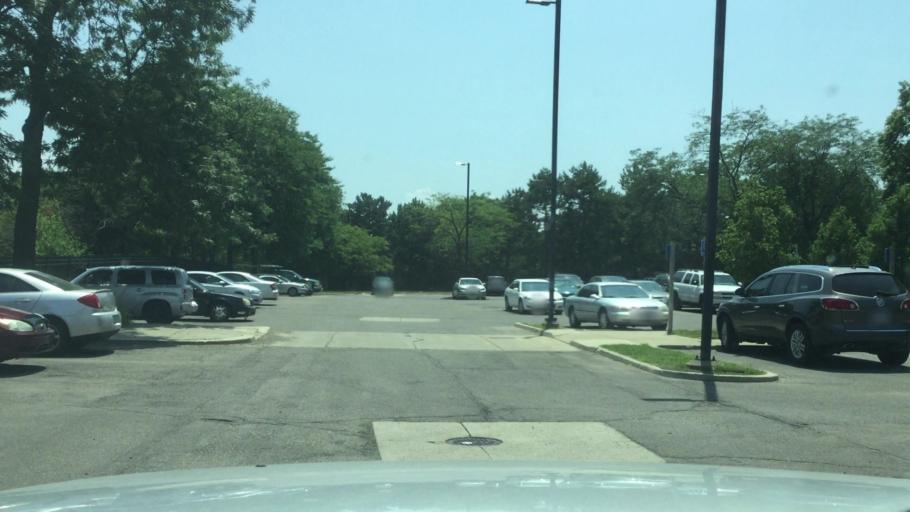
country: US
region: Michigan
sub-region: Wayne County
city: Detroit
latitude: 42.3458
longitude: -83.0218
